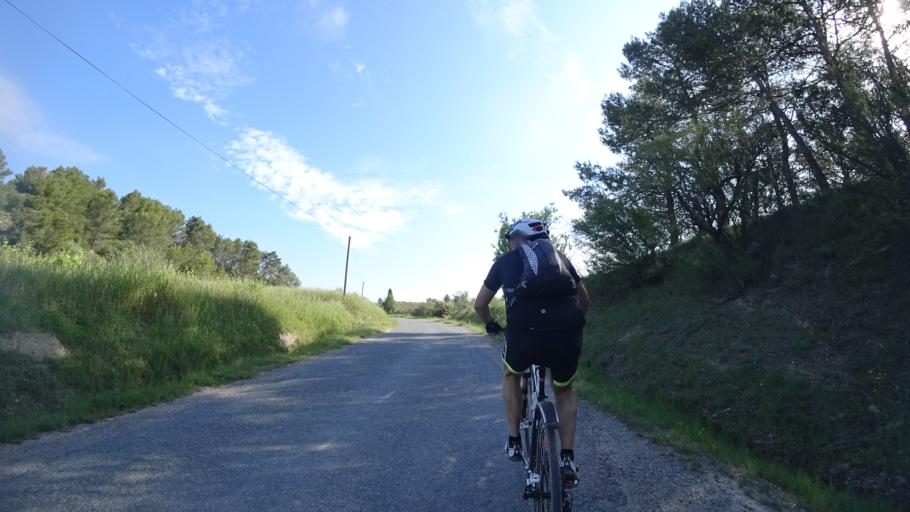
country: FR
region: Languedoc-Roussillon
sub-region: Departement de l'Herault
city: Olonzac
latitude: 43.2460
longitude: 2.7217
